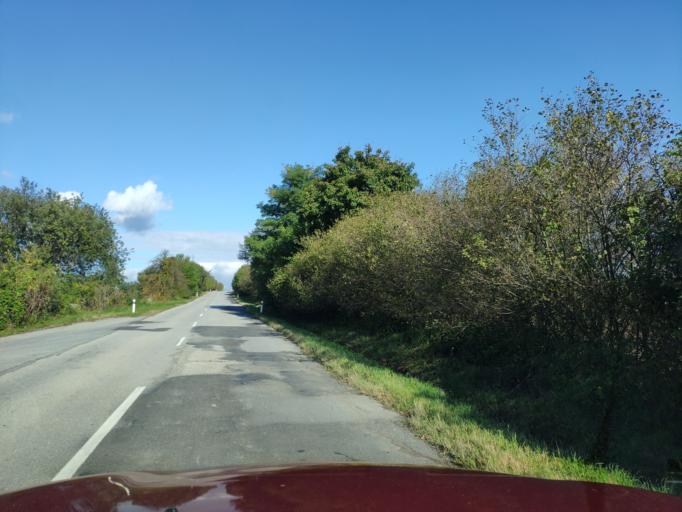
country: SK
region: Presovsky
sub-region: Okres Presov
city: Presov
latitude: 48.8901
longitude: 21.2606
